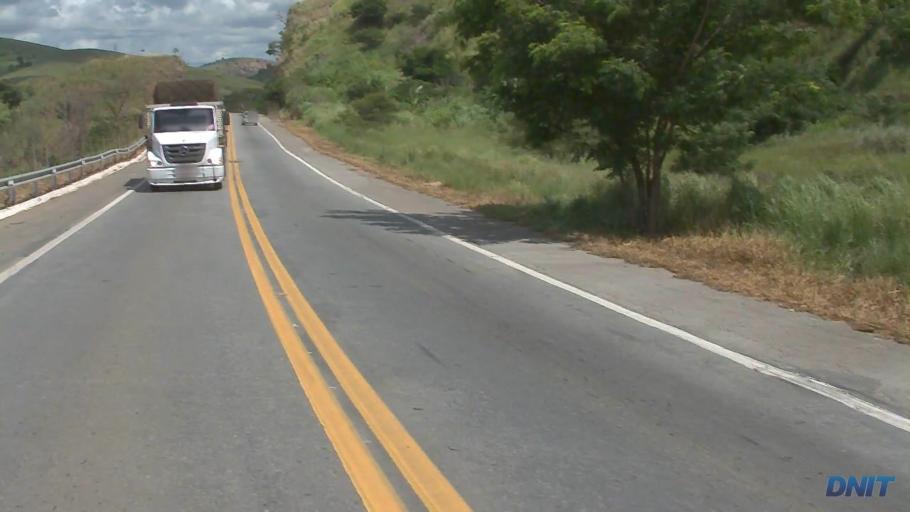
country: BR
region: Minas Gerais
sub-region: Governador Valadares
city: Governador Valadares
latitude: -18.9287
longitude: -42.0428
